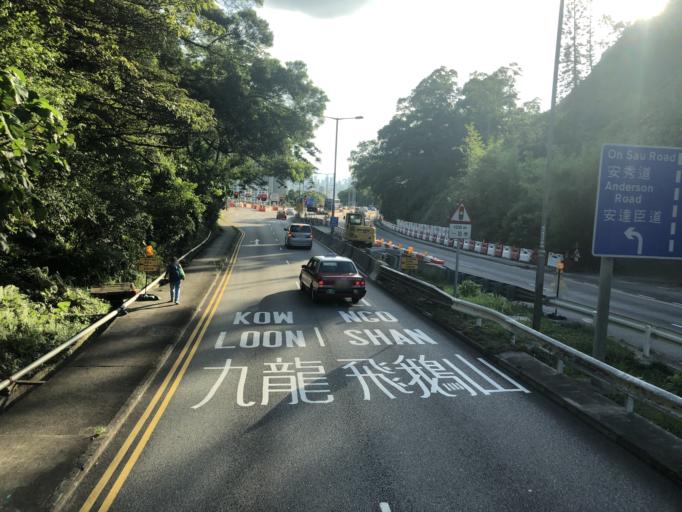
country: HK
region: Wong Tai Sin
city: Wong Tai Sin
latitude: 22.3345
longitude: 114.2298
